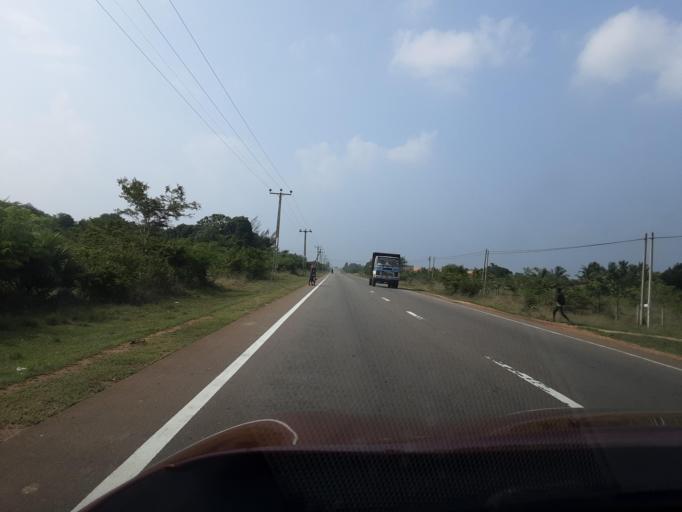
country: LK
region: Northern Province
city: Kilinochchi
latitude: 9.0828
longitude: 80.4799
